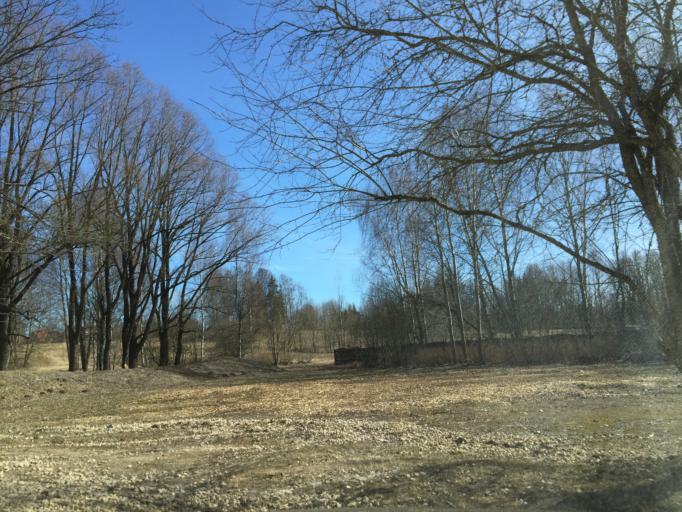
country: LV
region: Sigulda
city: Sigulda
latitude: 57.1397
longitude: 24.8177
